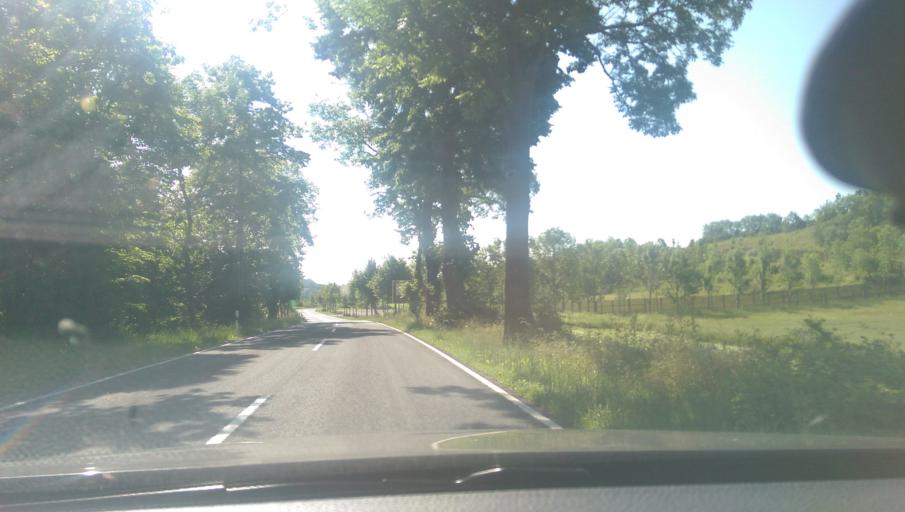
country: DE
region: Thuringia
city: Ifta
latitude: 51.0769
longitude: 10.1504
